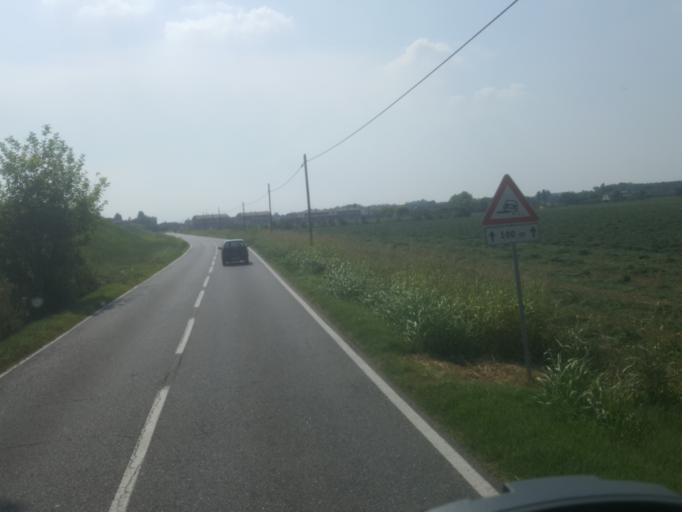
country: IT
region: Emilia-Romagna
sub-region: Provincia di Parma
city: Torrile
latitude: 44.9253
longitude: 10.3348
